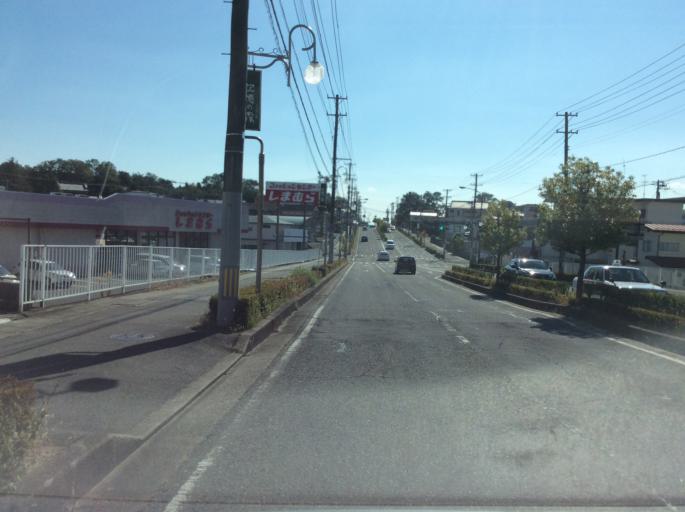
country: JP
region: Fukushima
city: Koriyama
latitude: 37.3832
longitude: 140.3600
